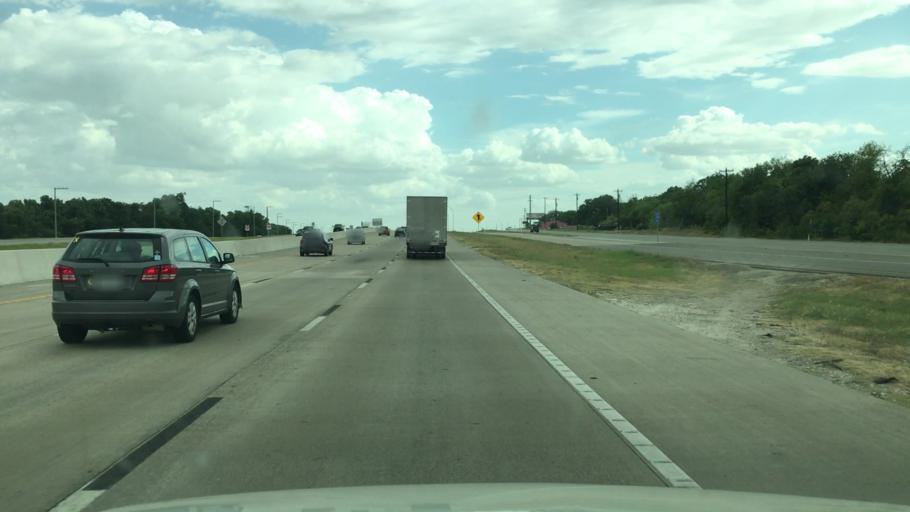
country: US
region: Texas
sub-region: McLennan County
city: Lorena
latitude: 31.3684
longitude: -97.2163
